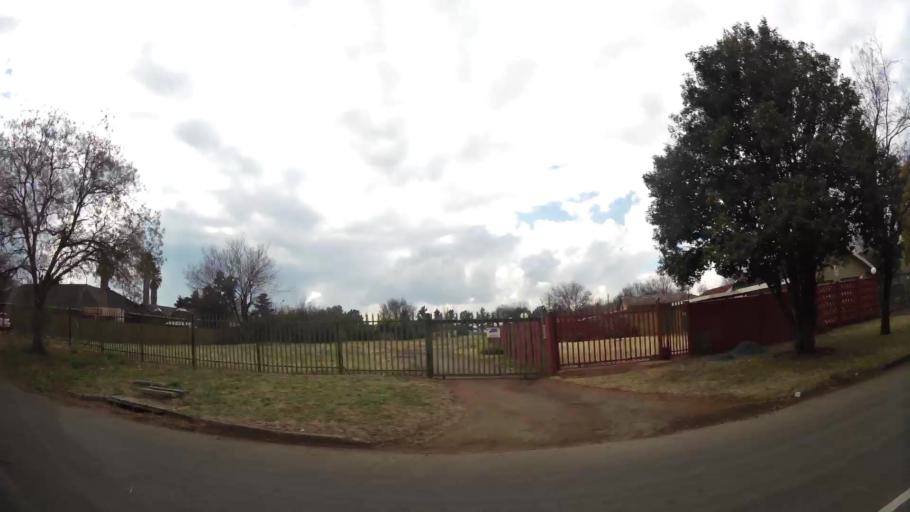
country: ZA
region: Gauteng
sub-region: Sedibeng District Municipality
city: Vereeniging
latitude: -26.6423
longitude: 27.9807
